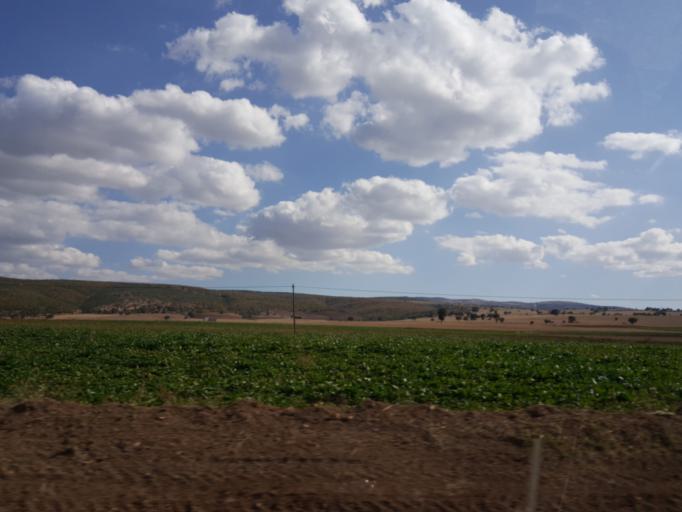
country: TR
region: Tokat
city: Sulusaray
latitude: 40.0038
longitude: 36.1401
